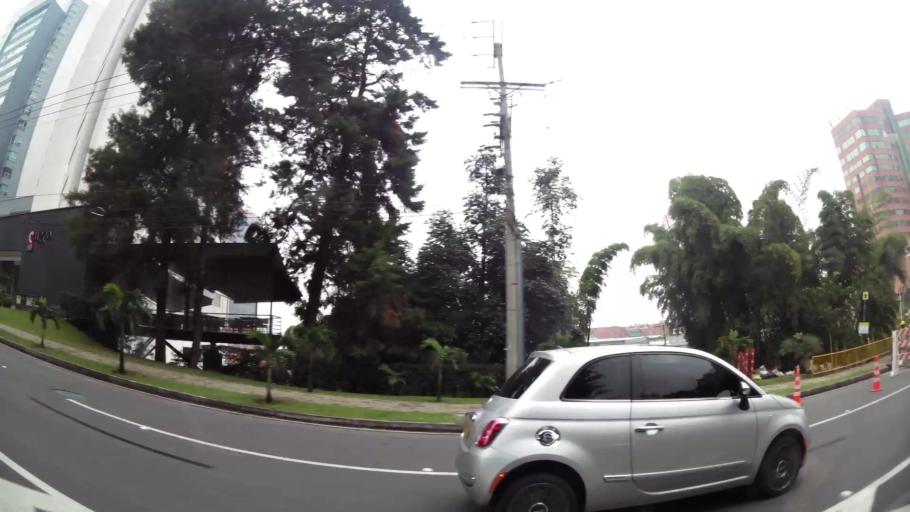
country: CO
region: Antioquia
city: Envigado
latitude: 6.1967
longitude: -75.5583
